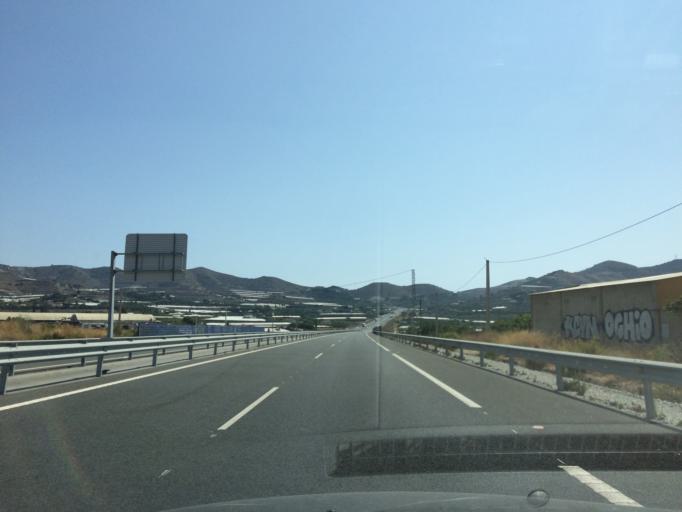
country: ES
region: Andalusia
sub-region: Provincia de Granada
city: El Varadero
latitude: 36.7309
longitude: -3.4754
